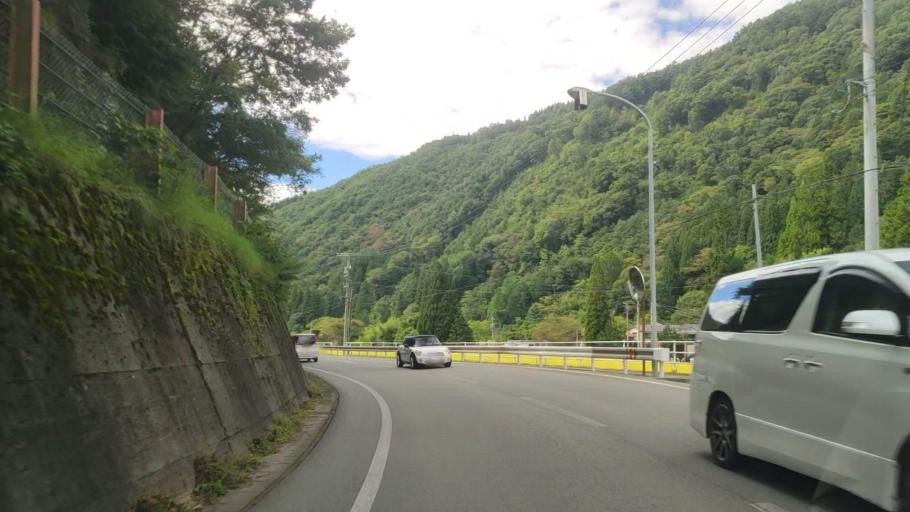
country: JP
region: Gifu
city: Takayama
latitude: 36.1814
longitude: 137.2783
